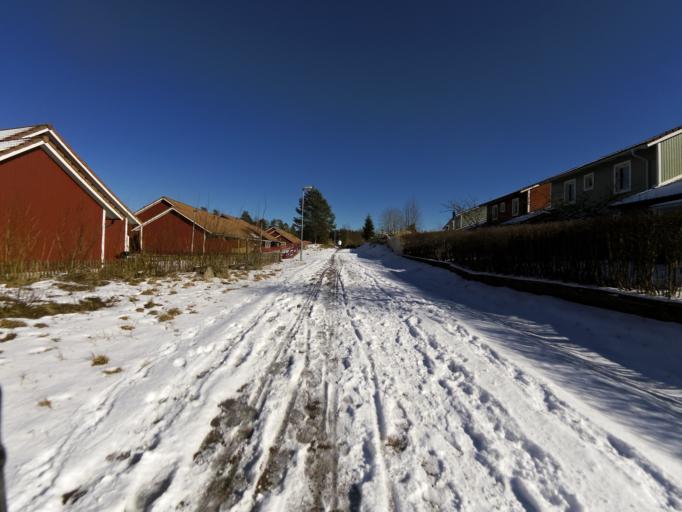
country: SE
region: Gaevleborg
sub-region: Gavle Kommun
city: Gavle
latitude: 60.6615
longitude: 17.2263
